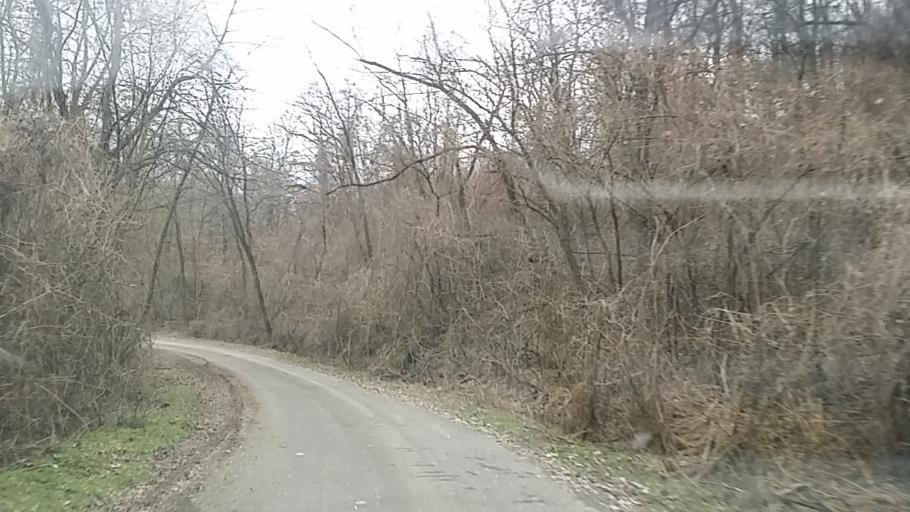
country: HU
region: Borsod-Abauj-Zemplen
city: Rudabanya
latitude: 48.3974
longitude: 20.6485
